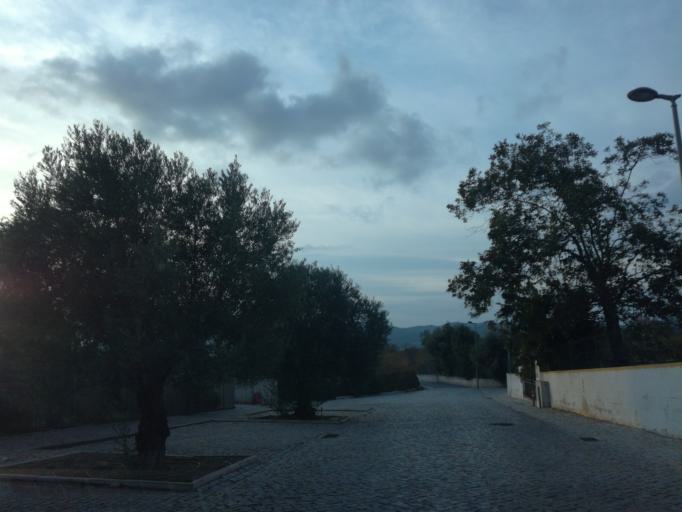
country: PT
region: Faro
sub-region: Sao Bras de Alportel
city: Sao Bras de Alportel
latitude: 37.0975
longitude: -7.8969
